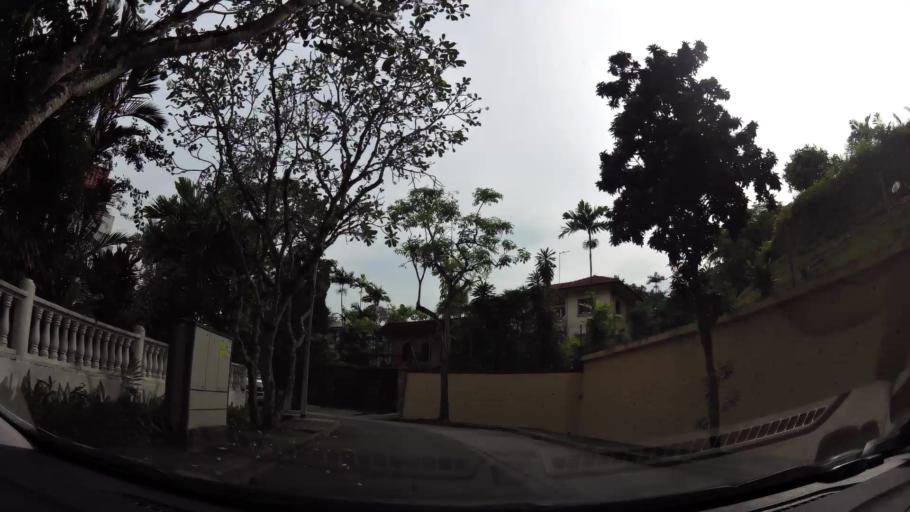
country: SG
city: Singapore
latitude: 1.3205
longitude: 103.7940
